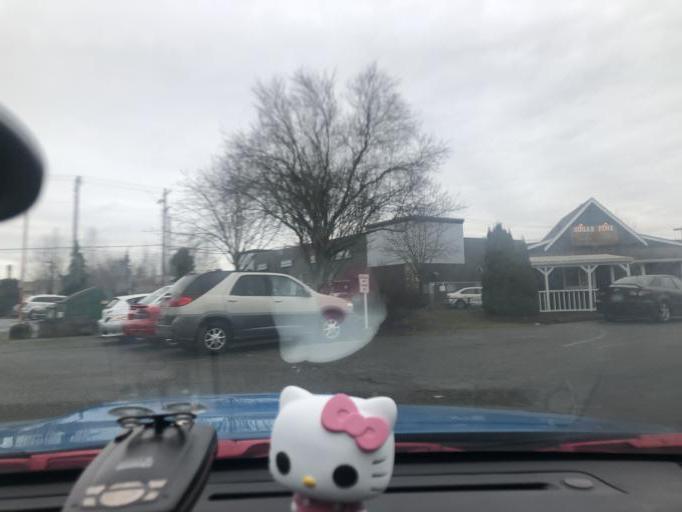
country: US
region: Washington
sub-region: Snohomish County
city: Smokey Point
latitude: 48.1491
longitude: -122.1818
